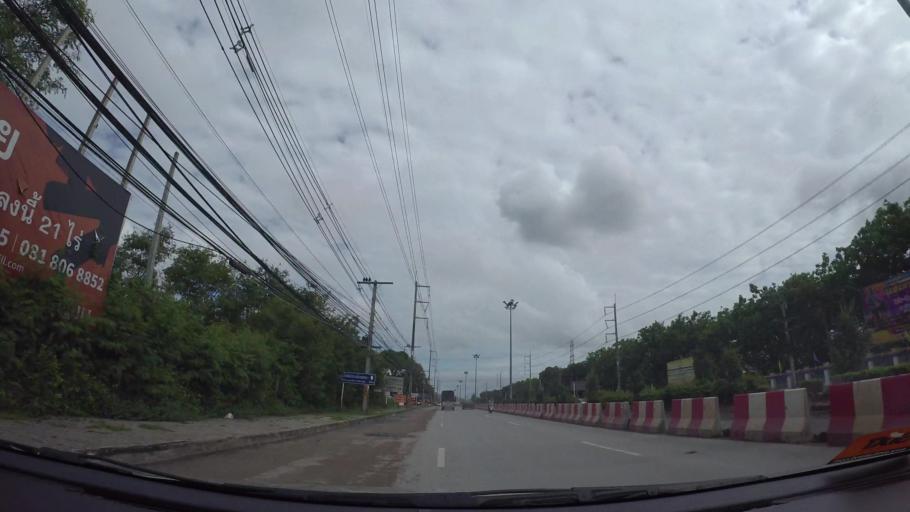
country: TH
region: Rayong
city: Rayong
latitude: 12.7045
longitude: 101.1831
